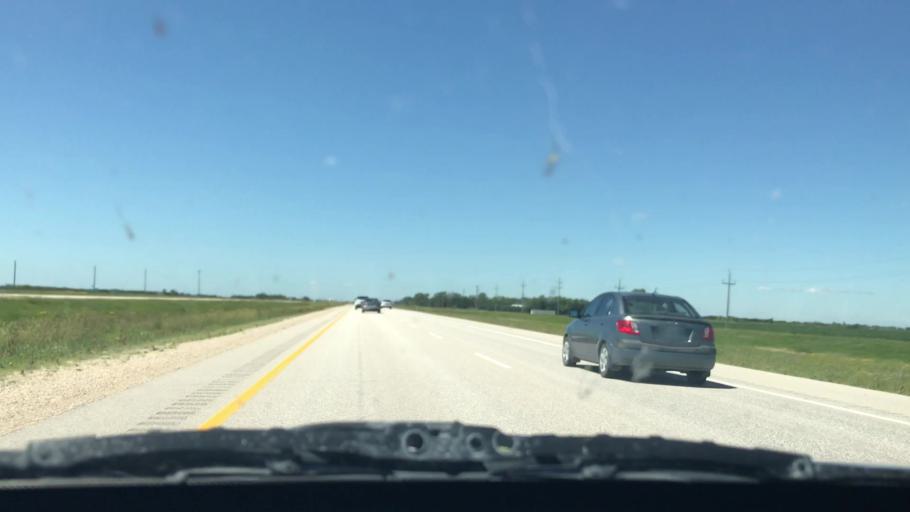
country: CA
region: Manitoba
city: Steinbach
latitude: 49.7376
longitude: -96.7374
